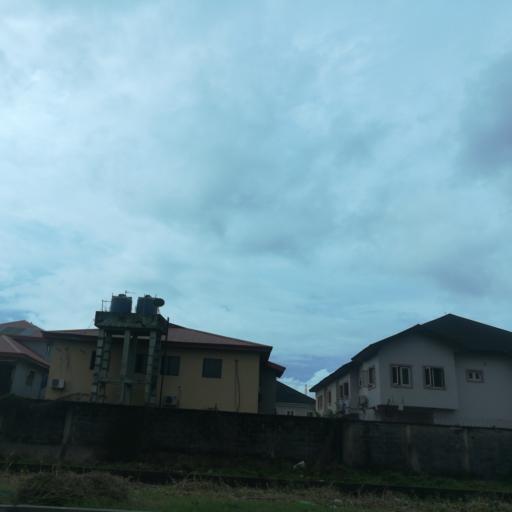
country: NG
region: Lagos
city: Ikoyi
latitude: 6.4371
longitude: 3.4674
